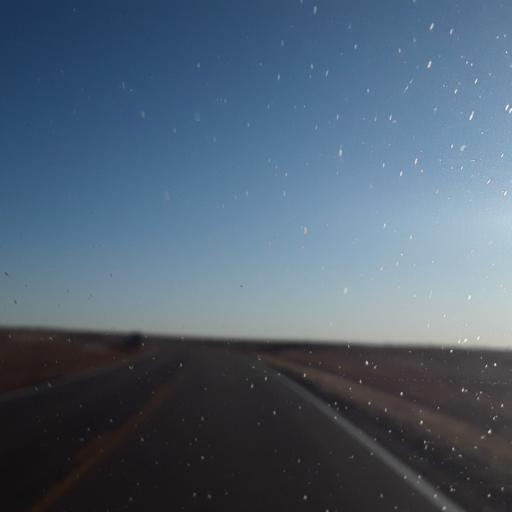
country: US
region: Kansas
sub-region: Wallace County
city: Sharon Springs
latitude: 39.0991
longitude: -101.7372
